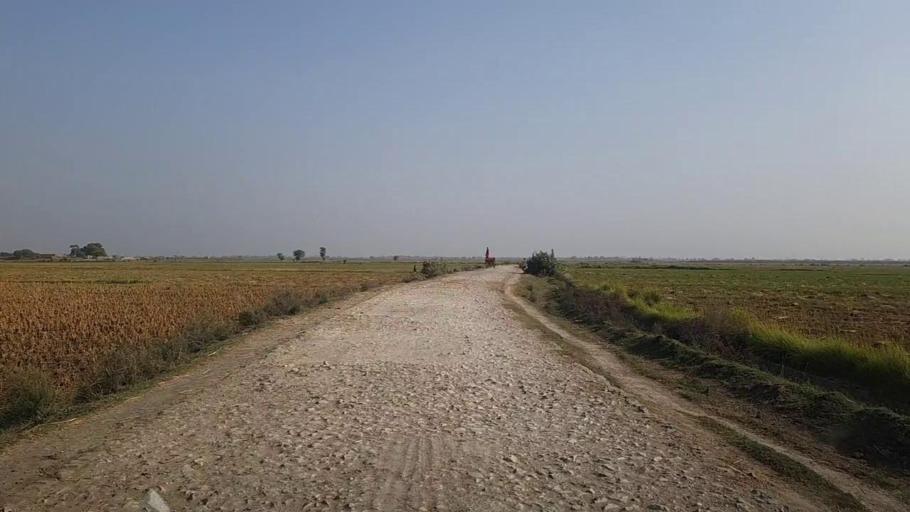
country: PK
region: Sindh
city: Kandhkot
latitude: 28.3025
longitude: 69.2493
